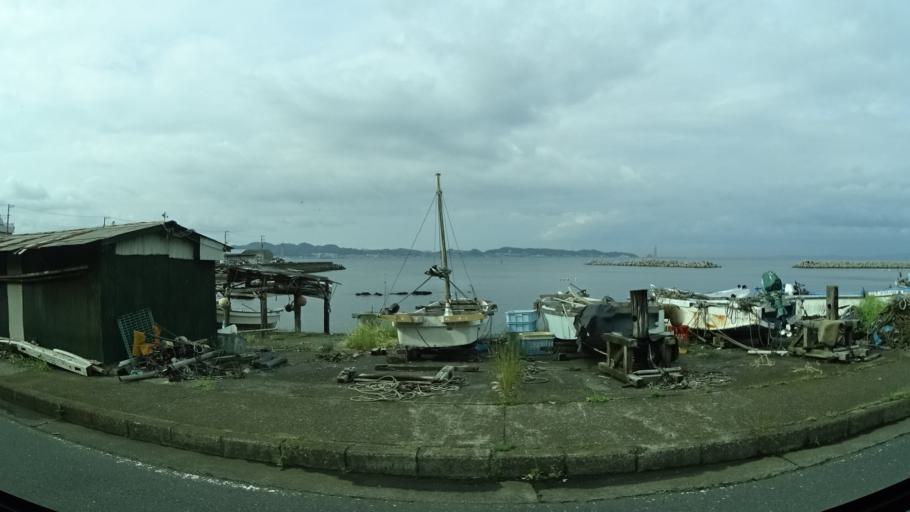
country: JP
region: Kanagawa
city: Miura
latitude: 35.1576
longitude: 139.6674
